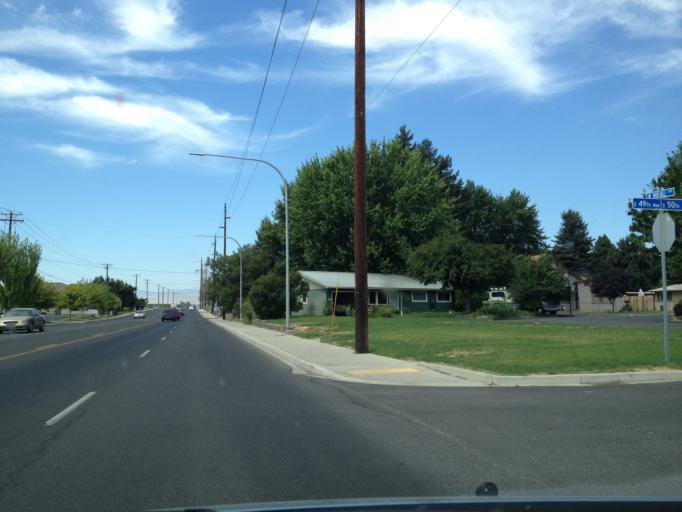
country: US
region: Washington
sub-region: Yakima County
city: West Valley
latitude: 46.5855
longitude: -120.5736
